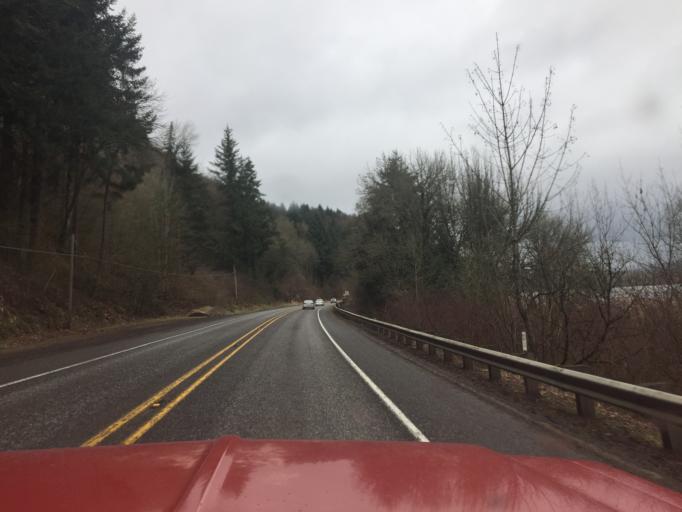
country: US
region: Washington
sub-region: Cowlitz County
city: Kalama
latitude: 46.0392
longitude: -122.8974
